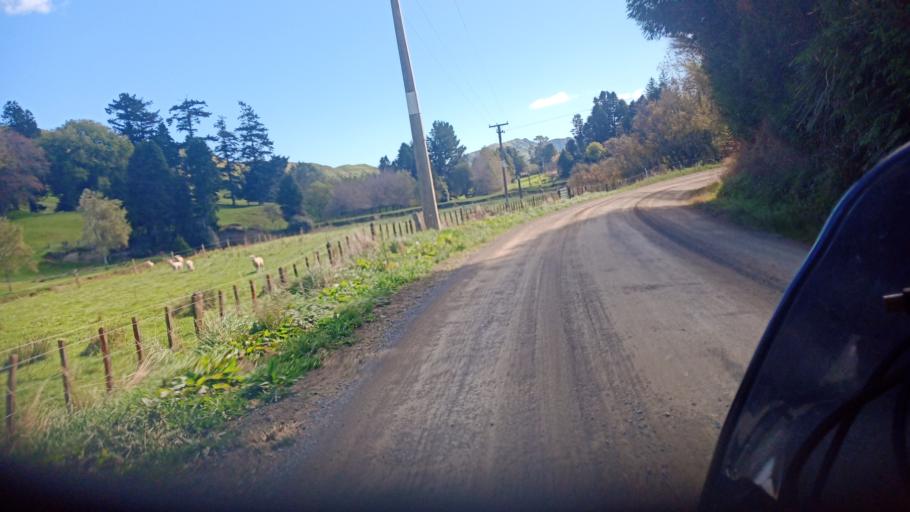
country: NZ
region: Bay of Plenty
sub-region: Opotiki District
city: Opotiki
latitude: -38.2967
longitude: 177.5526
